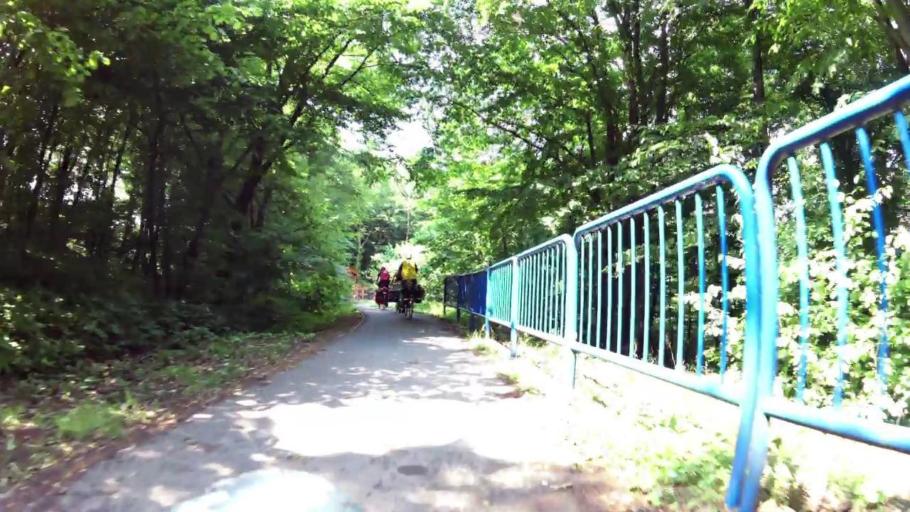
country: PL
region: Kujawsko-Pomorskie
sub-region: Powiat bydgoski
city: Koronowo
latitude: 53.2969
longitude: 17.9472
